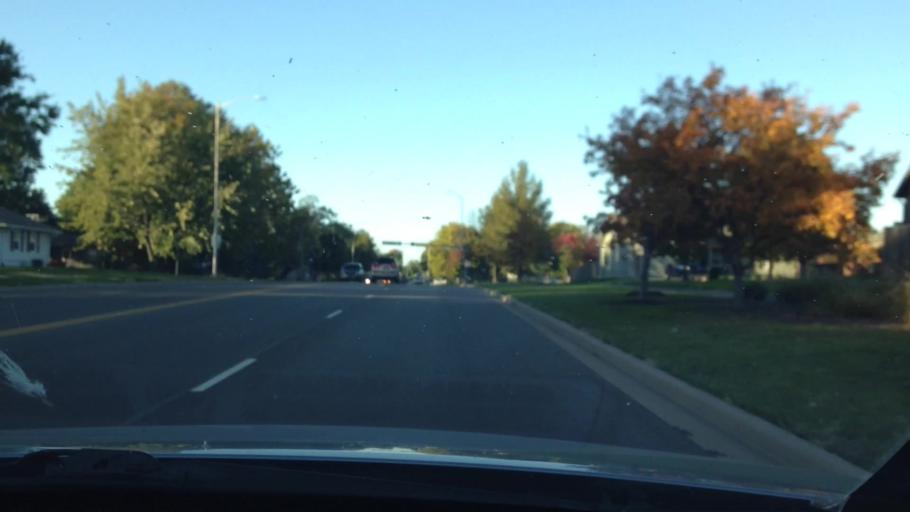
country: US
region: Kansas
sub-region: Johnson County
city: Gardner
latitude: 38.8013
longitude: -94.9275
